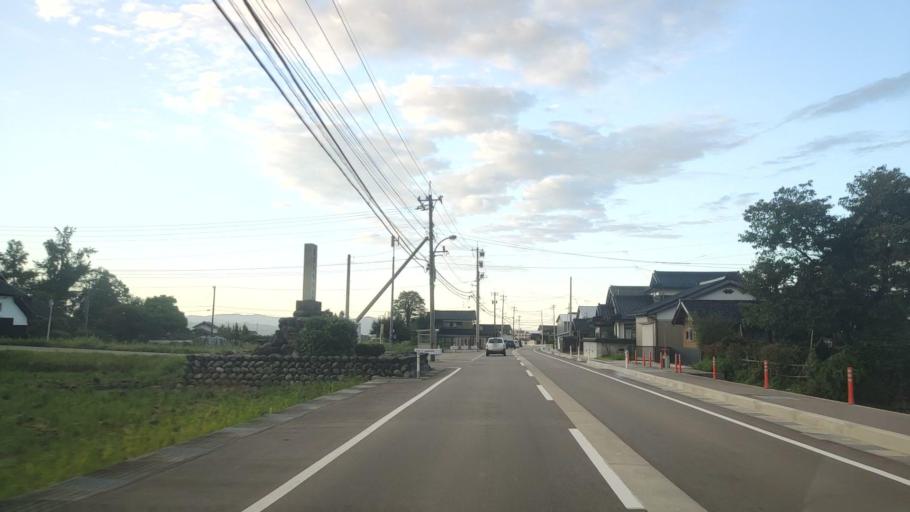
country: JP
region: Toyama
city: Nanto-shi
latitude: 36.6104
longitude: 136.8900
